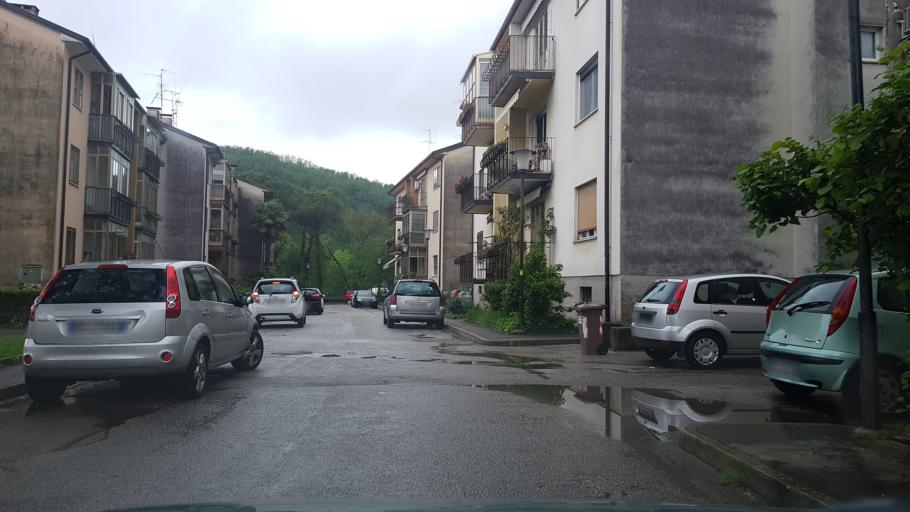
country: IT
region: Friuli Venezia Giulia
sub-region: Provincia di Gorizia
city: Gorizia
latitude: 45.9566
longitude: 13.6100
